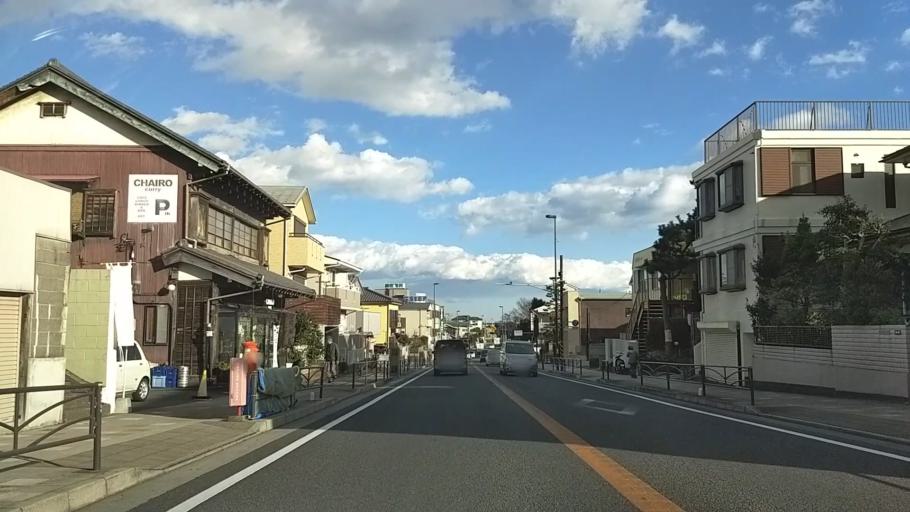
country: JP
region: Kanagawa
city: Oiso
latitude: 35.3079
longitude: 139.3099
